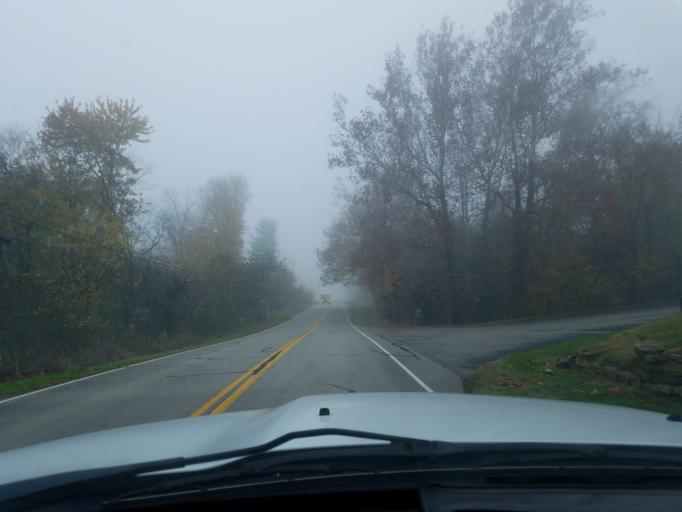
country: US
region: Indiana
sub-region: Floyd County
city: New Albany
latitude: 38.3261
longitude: -85.8785
